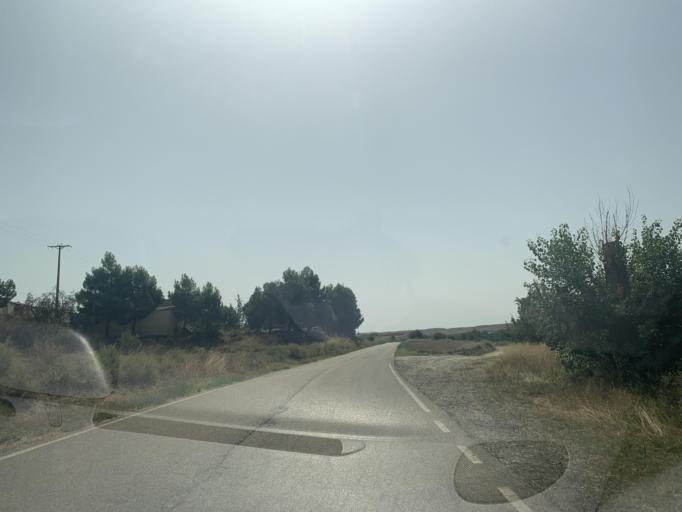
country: ES
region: Aragon
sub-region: Provincia de Zaragoza
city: Almonacid de la Cuba
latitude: 41.2736
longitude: -0.7853
